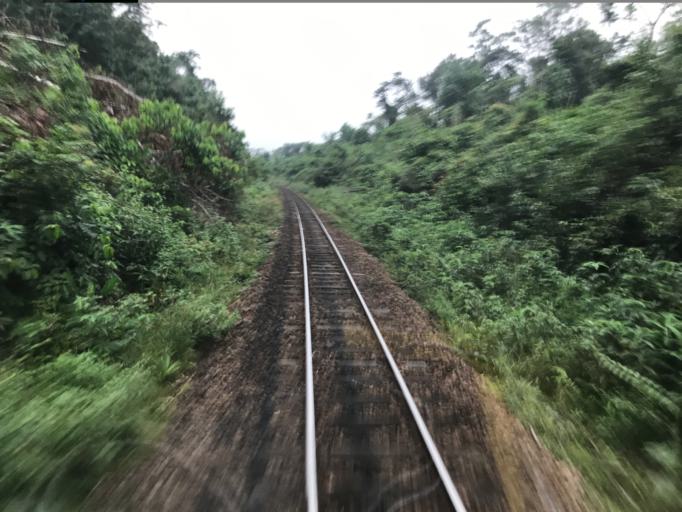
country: CM
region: Littoral
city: Edea
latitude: 3.9659
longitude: 10.0818
